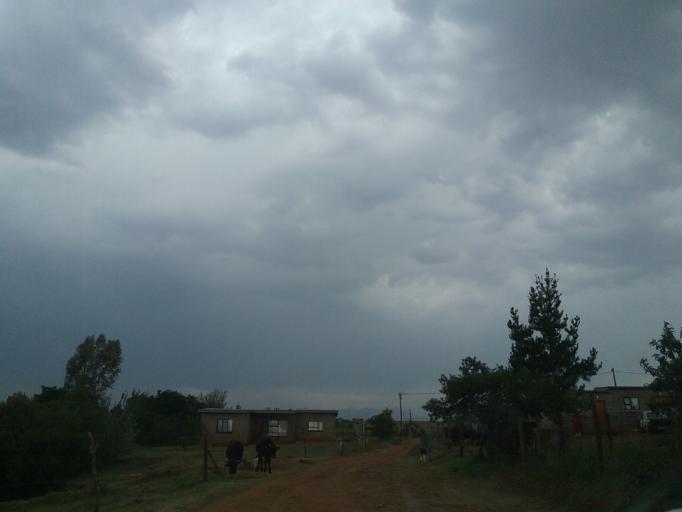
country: LS
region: Maseru
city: Maseru
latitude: -29.4208
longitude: 27.5686
